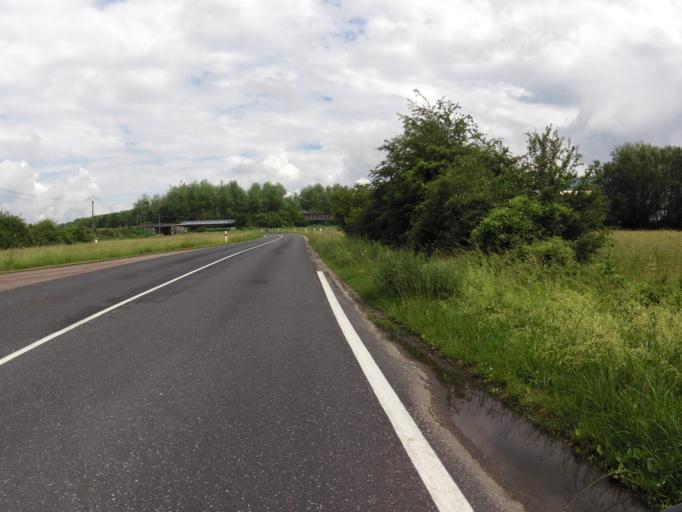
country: FR
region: Lorraine
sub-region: Departement de la Meuse
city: Revigny-sur-Ornain
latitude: 48.8104
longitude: 4.9633
